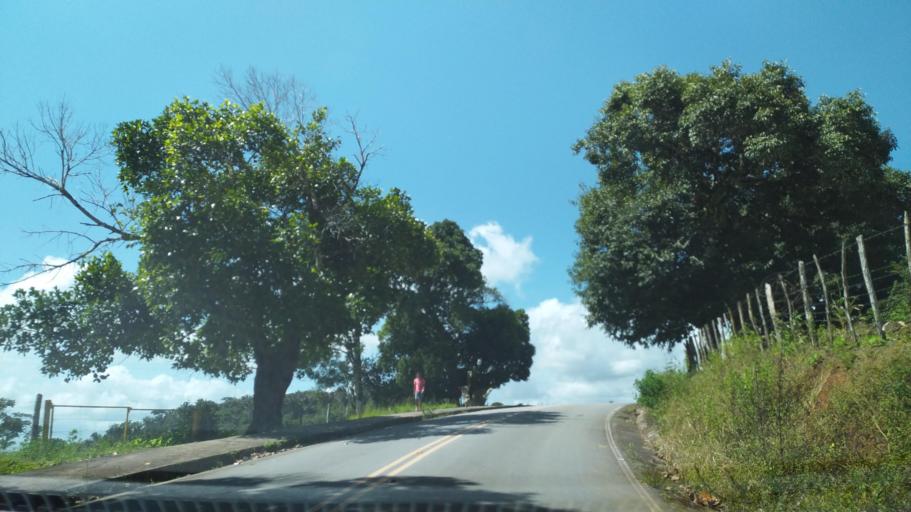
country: BR
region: Alagoas
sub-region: Uniao Dos Palmares
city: Uniao dos Palmares
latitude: -9.1624
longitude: -36.0717
